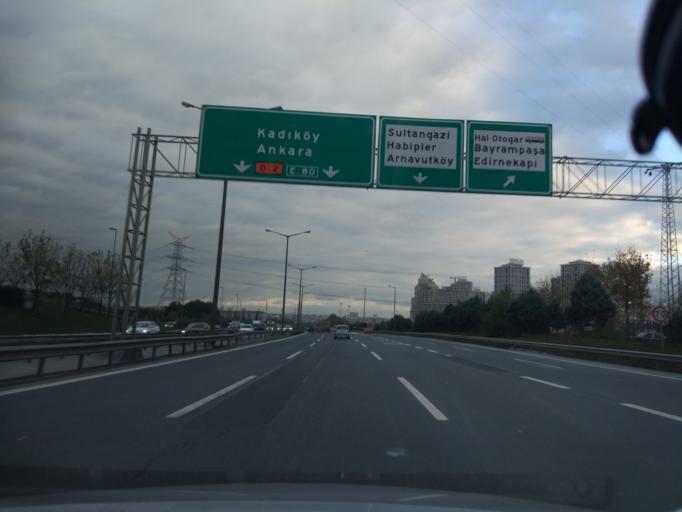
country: TR
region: Istanbul
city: Sultangazi
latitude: 41.0749
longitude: 28.8701
